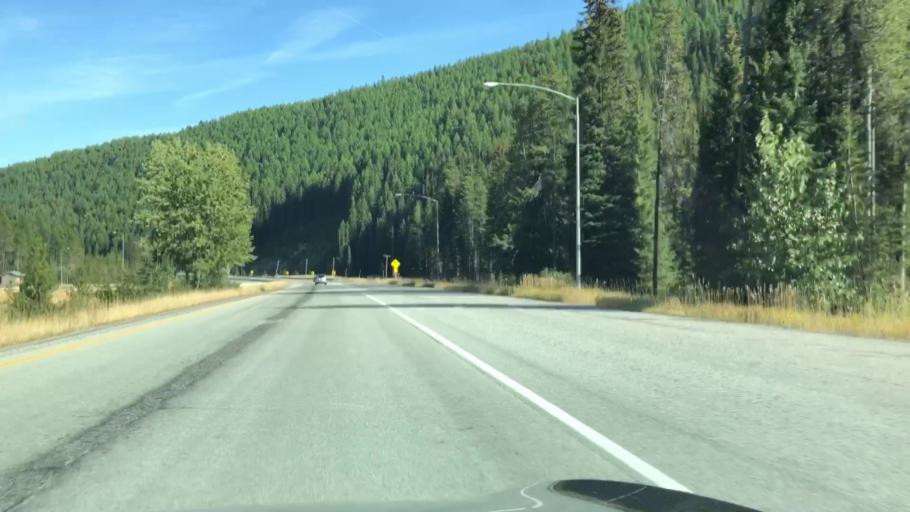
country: US
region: Idaho
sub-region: Shoshone County
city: Wallace
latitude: 47.4197
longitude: -115.6277
